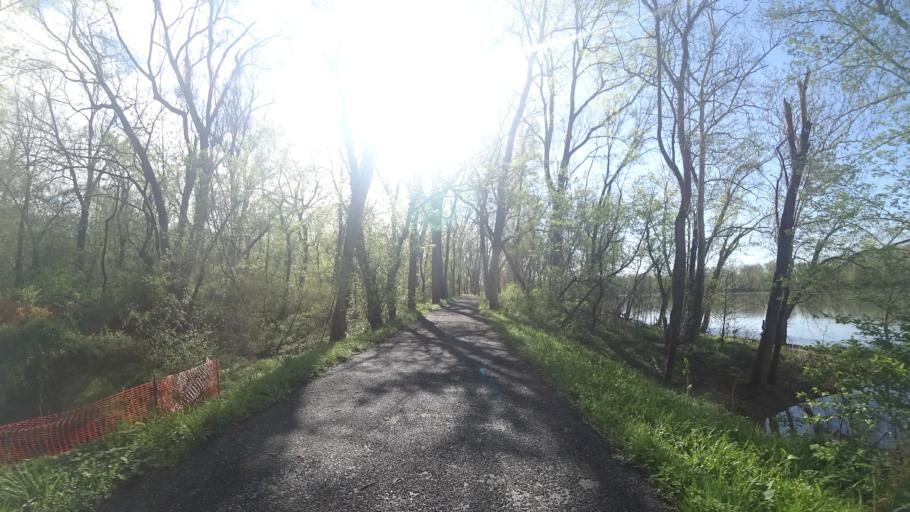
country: US
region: Virginia
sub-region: Loudoun County
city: Countryside
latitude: 39.0725
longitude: -77.4129
